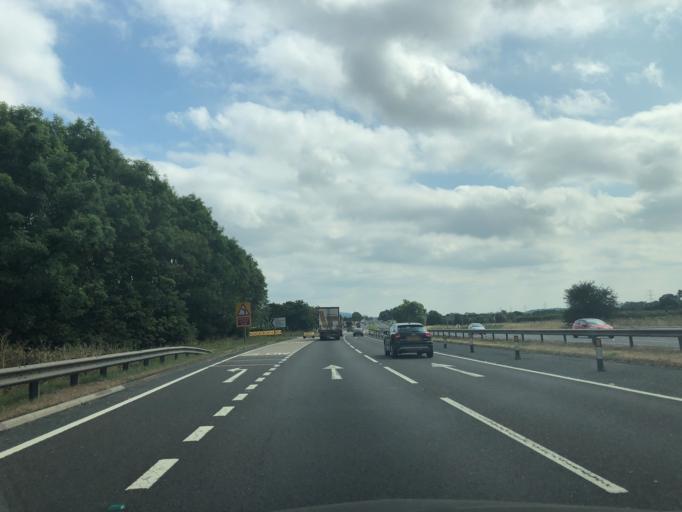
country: GB
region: England
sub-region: Stockton-on-Tees
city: Yarm
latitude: 54.4284
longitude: -1.3203
